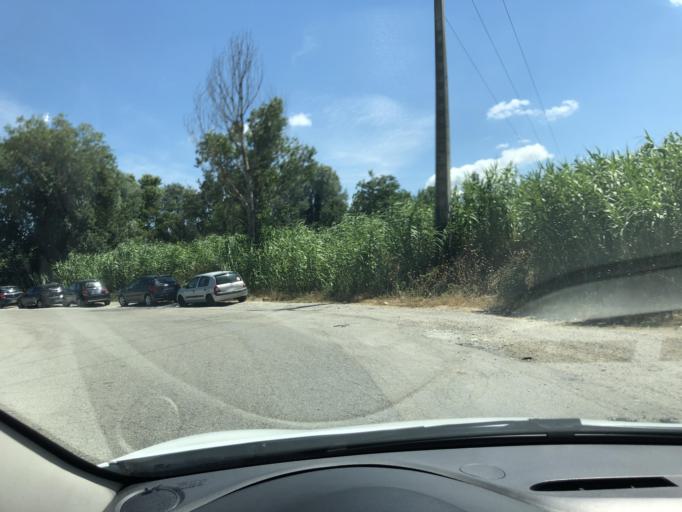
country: FR
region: Provence-Alpes-Cote d'Azur
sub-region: Departement des Bouches-du-Rhone
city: Chateaurenard
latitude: 43.8929
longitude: 4.8777
